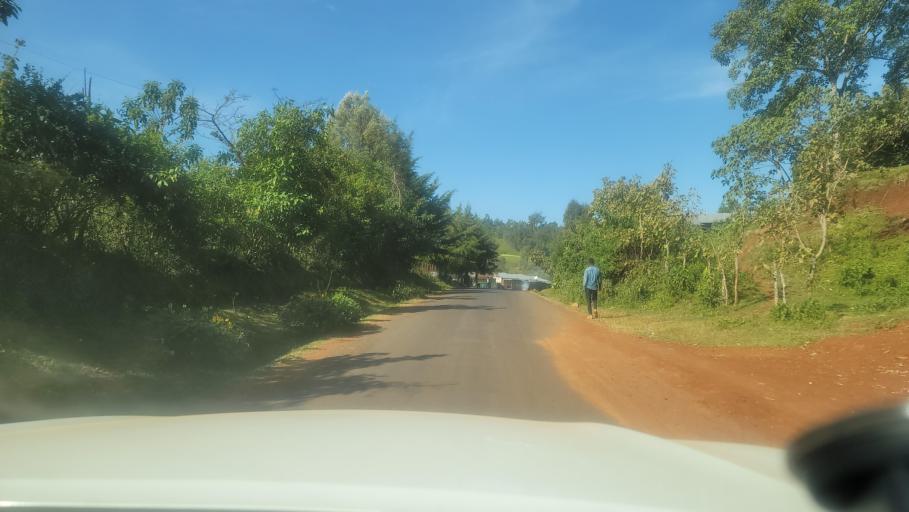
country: ET
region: Oromiya
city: Agaro
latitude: 7.7996
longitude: 36.4739
